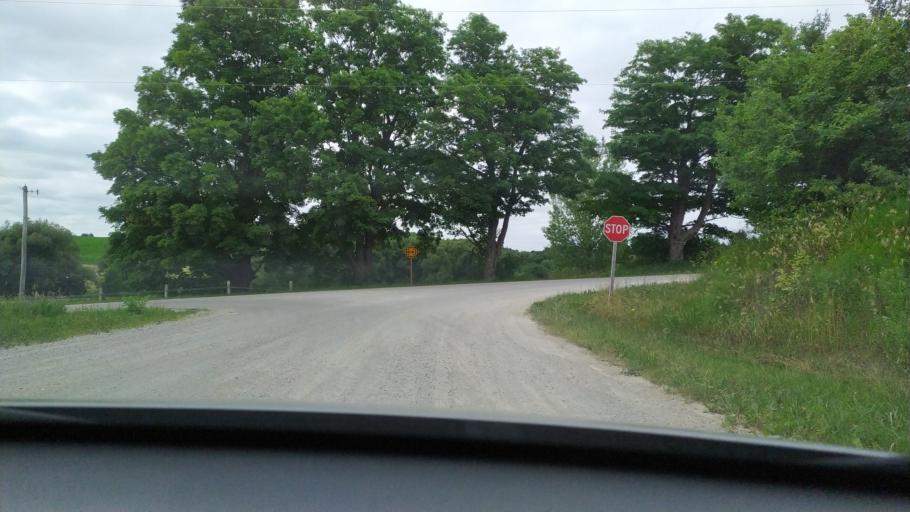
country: CA
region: Ontario
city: Stratford
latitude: 43.2774
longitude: -80.9792
